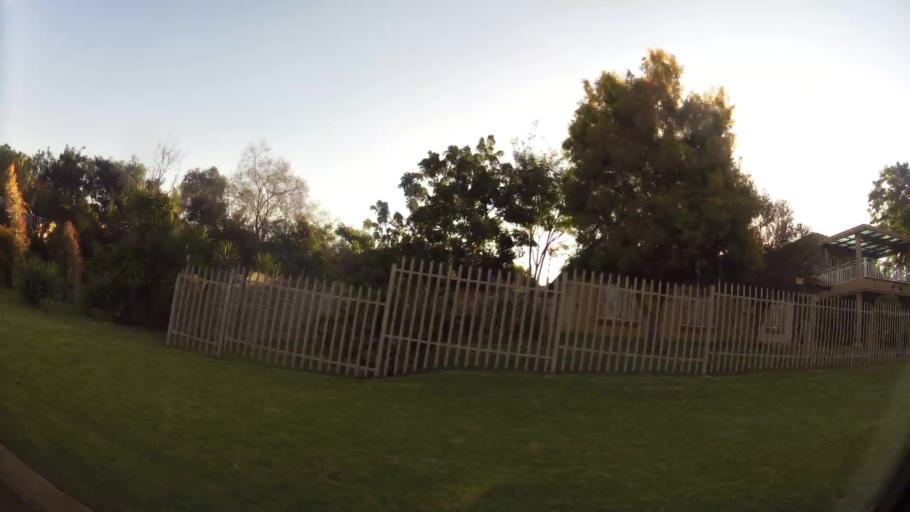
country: ZA
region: North-West
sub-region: Bojanala Platinum District Municipality
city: Rustenburg
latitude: -25.7146
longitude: 27.2373
